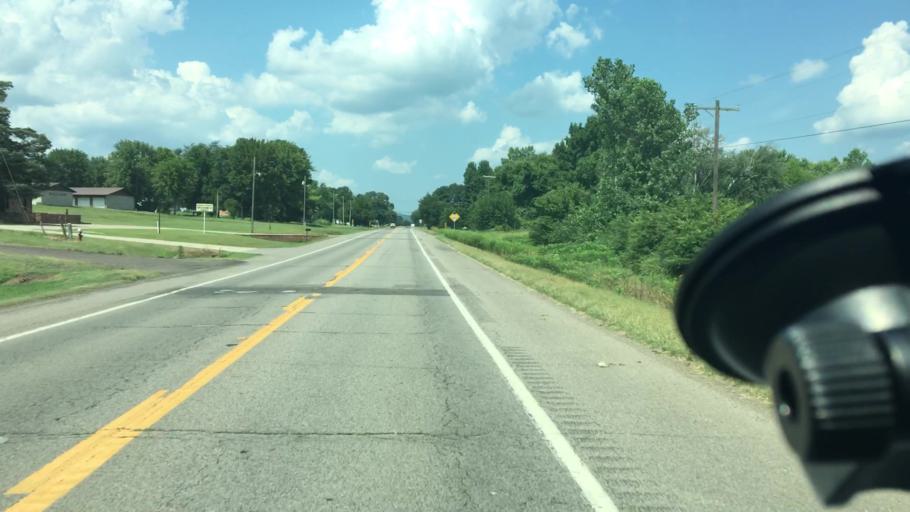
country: US
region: Arkansas
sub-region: Logan County
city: Paris
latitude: 35.2939
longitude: -93.6964
